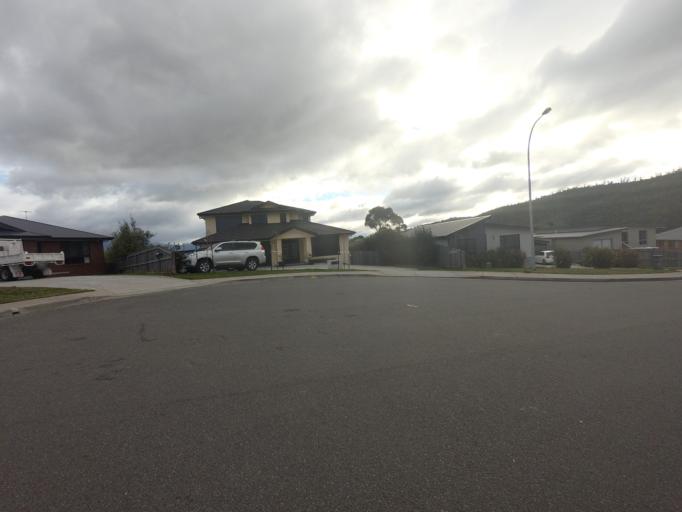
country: AU
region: Tasmania
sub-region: Clarence
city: Warrane
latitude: -42.8595
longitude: 147.4090
